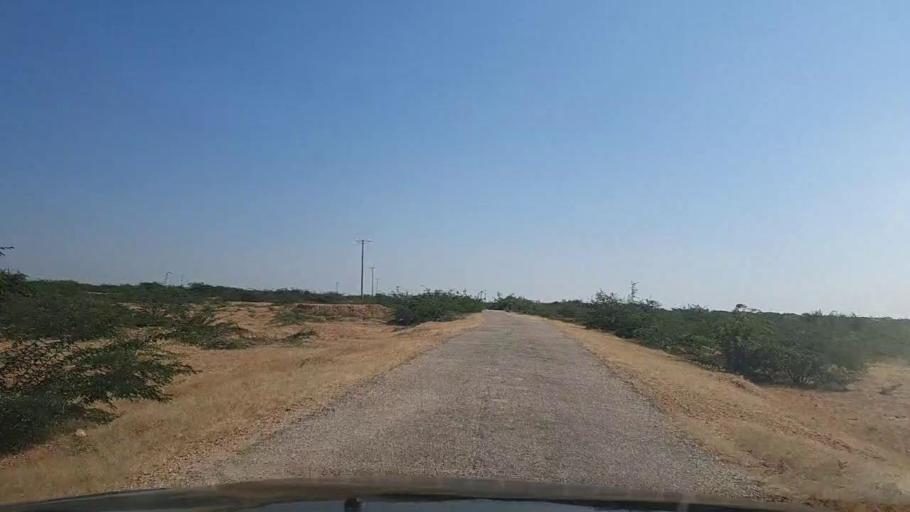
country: PK
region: Sindh
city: Thatta
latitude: 24.6295
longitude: 67.8385
